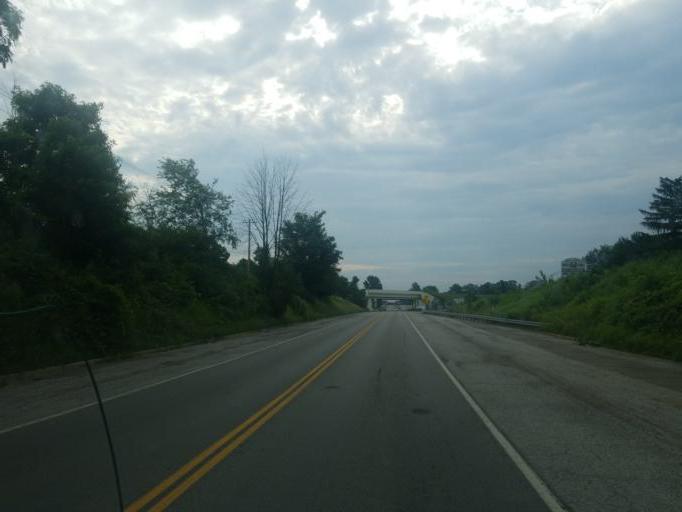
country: US
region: Ohio
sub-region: Wayne County
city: Apple Creek
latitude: 40.7958
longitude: -81.8142
